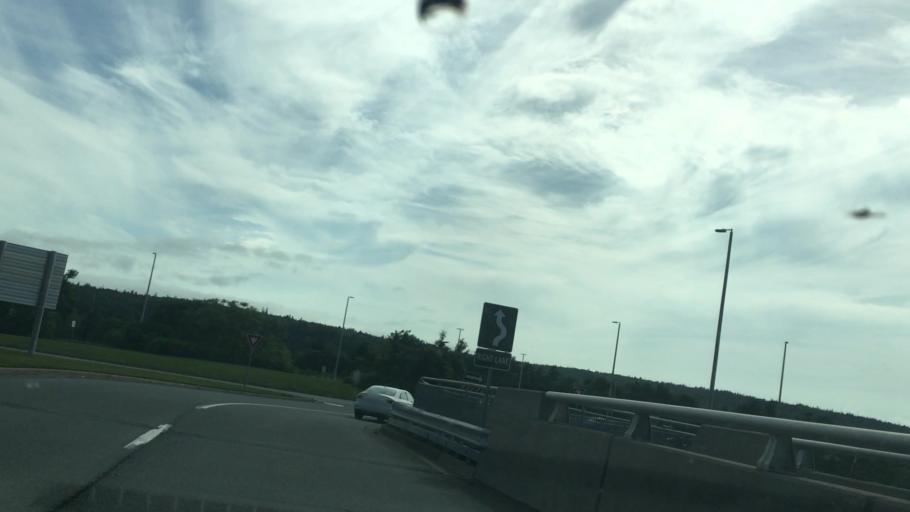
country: CA
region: Nova Scotia
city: Dartmouth
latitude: 44.6988
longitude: -63.6911
